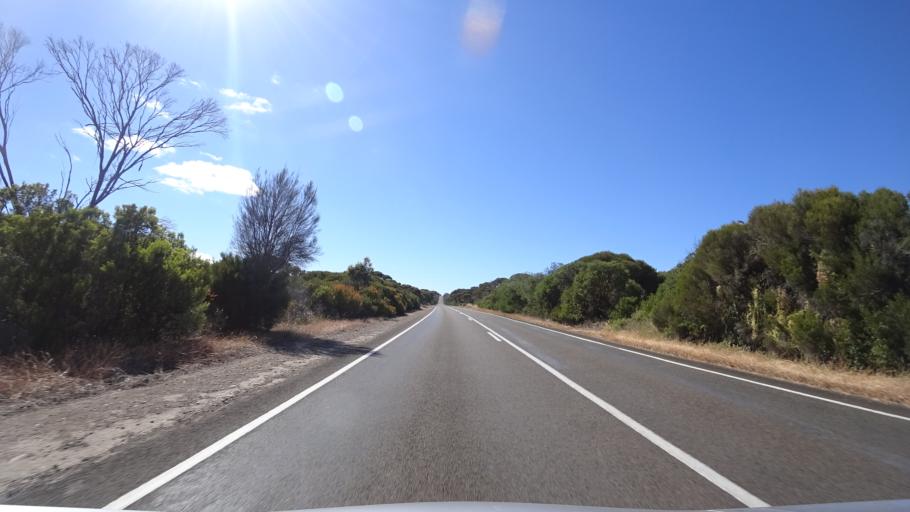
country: AU
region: South Australia
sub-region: Kangaroo Island
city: Kingscote
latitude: -35.7568
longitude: 137.6032
